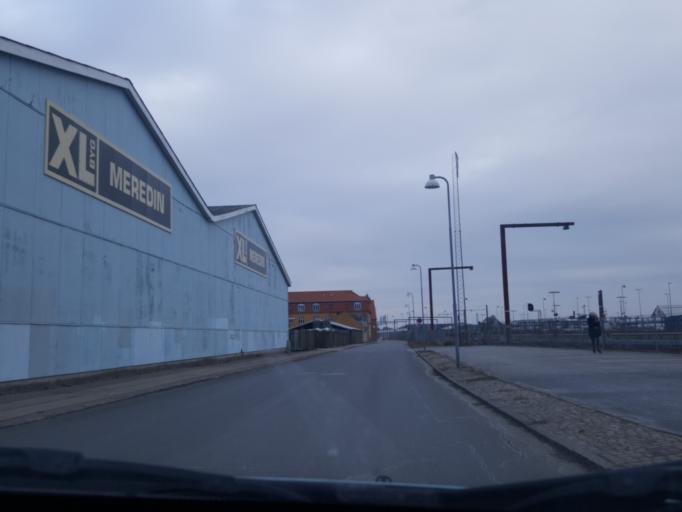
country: DK
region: Zealand
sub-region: Kalundborg Kommune
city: Kalundborg
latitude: 55.6780
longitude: 11.0917
